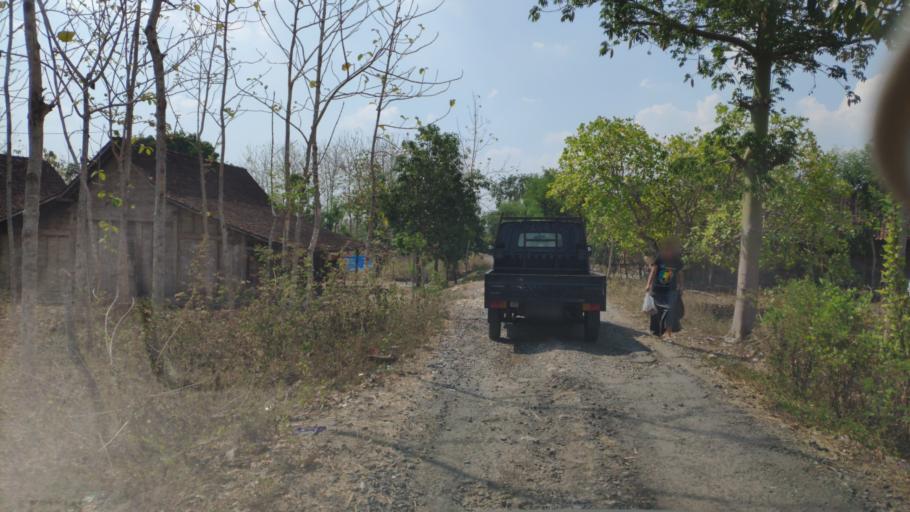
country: ID
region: Central Java
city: Botoh
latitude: -7.0893
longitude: 111.4735
